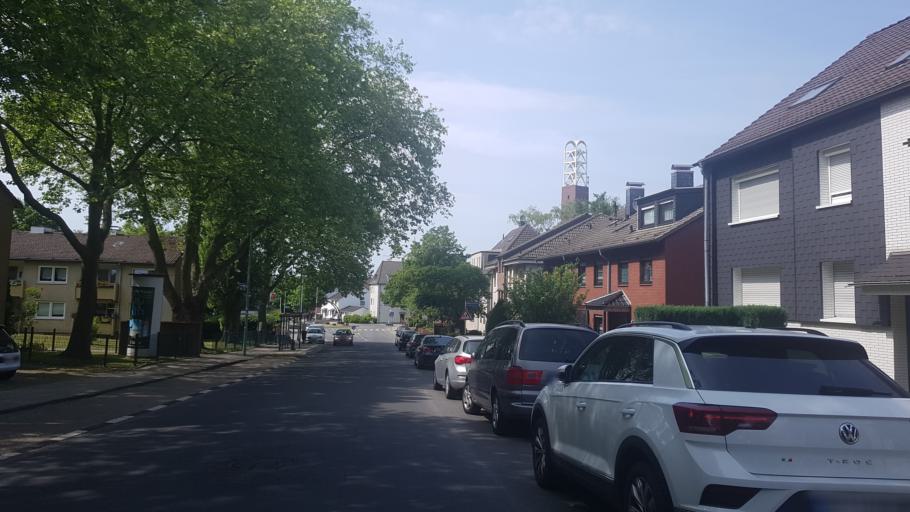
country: DE
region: North Rhine-Westphalia
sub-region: Regierungsbezirk Dusseldorf
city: Oberhausen
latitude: 51.4645
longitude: 6.8960
